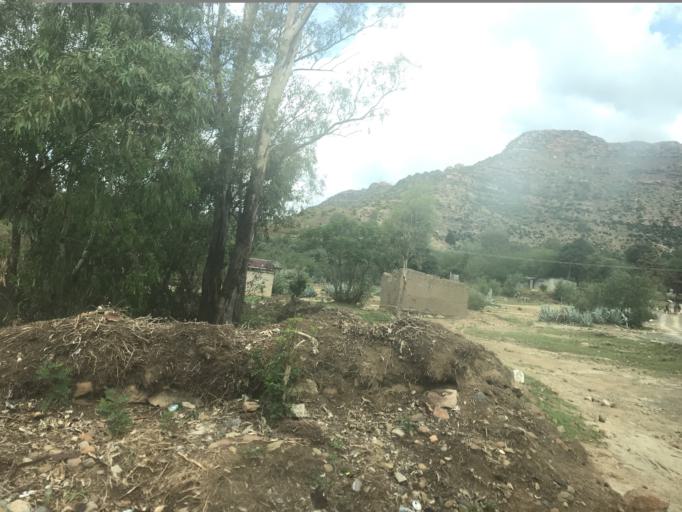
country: LS
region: Maseru
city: Nako
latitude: -29.6274
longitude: 27.5120
